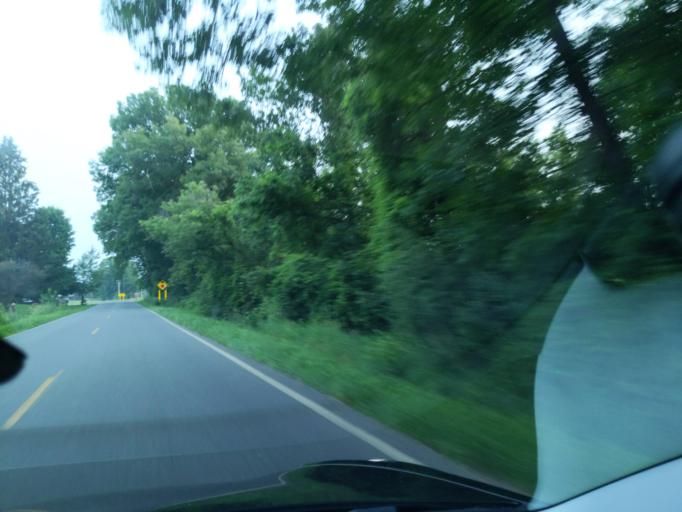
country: US
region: Michigan
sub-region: Jackson County
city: Jackson
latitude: 42.3362
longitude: -84.4877
